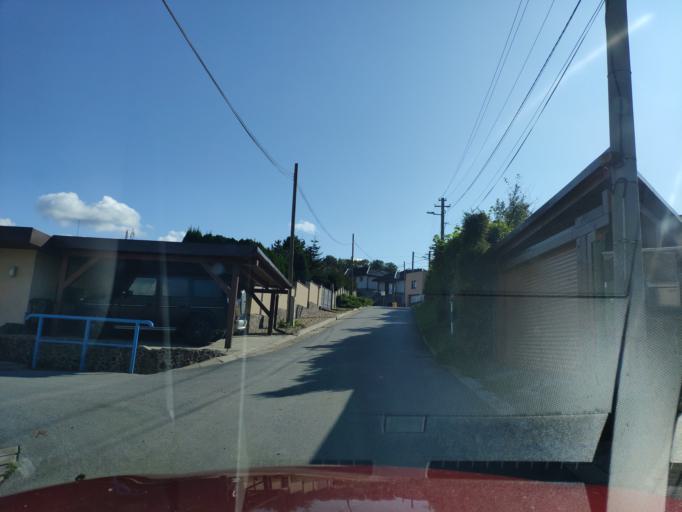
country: SK
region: Presovsky
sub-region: Okres Presov
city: Presov
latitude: 48.9413
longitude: 21.2910
